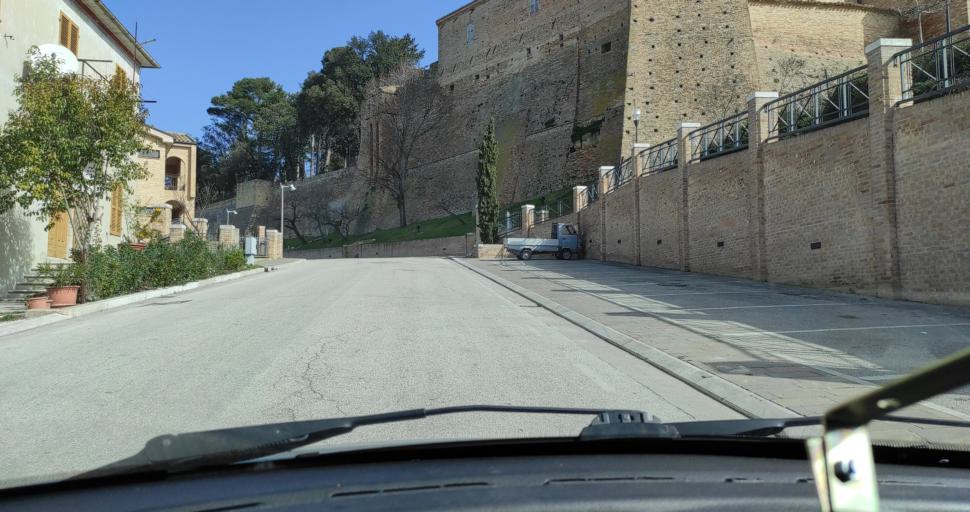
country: IT
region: The Marches
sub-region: Provincia di Macerata
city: Loro Piceno
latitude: 43.1655
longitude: 13.4152
